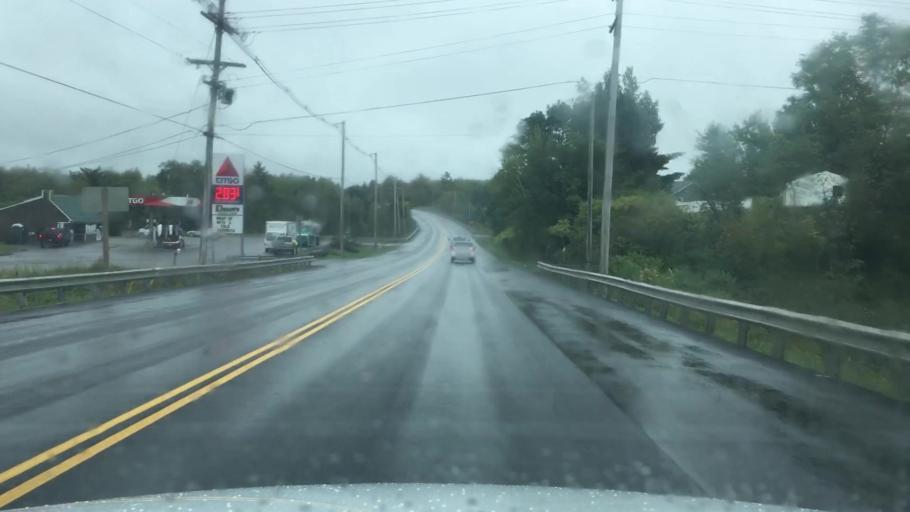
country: US
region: Maine
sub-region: Penobscot County
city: Hampden
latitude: 44.7706
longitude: -68.8572
